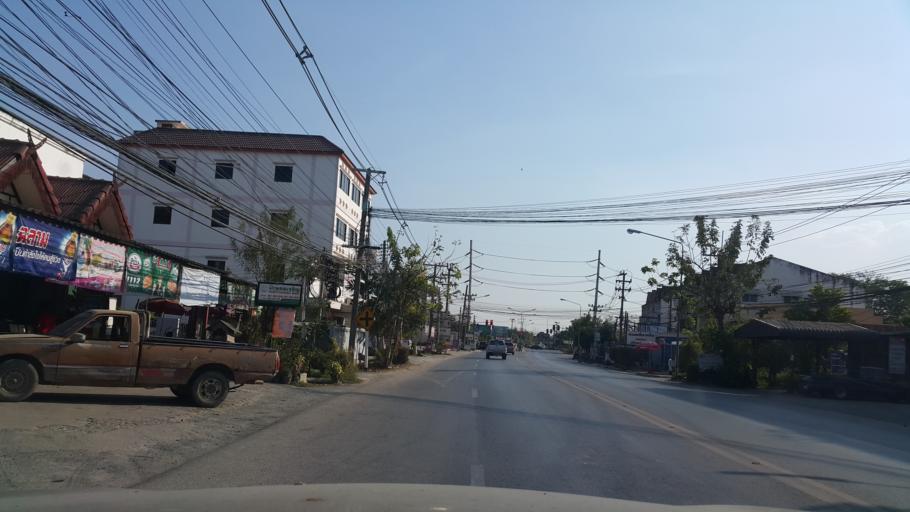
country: TH
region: Chiang Mai
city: San Sai
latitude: 18.8337
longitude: 99.0417
